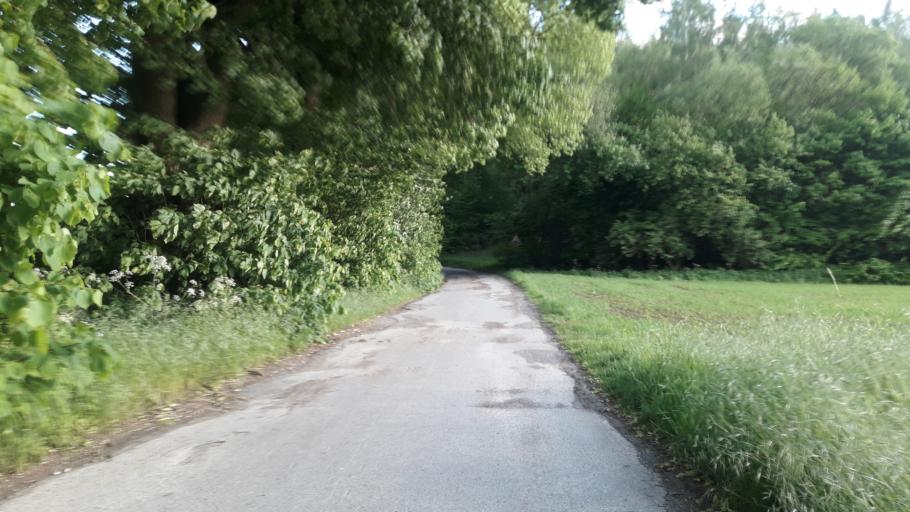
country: DE
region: North Rhine-Westphalia
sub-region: Regierungsbezirk Detmold
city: Paderborn
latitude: 51.6735
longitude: 8.7846
